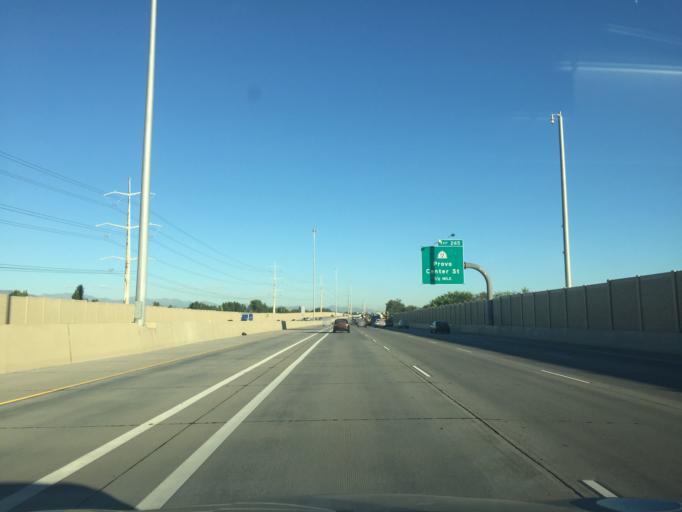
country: US
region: Utah
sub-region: Utah County
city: Provo
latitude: 40.2214
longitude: -111.6716
